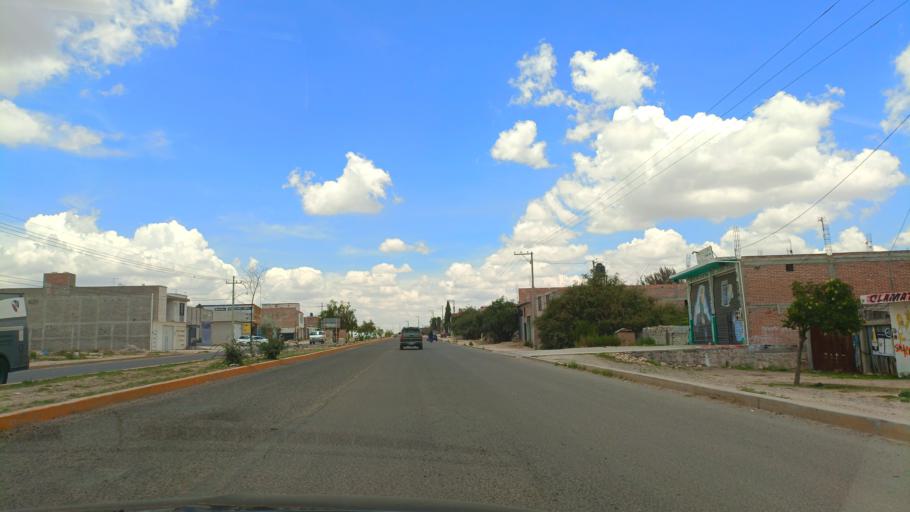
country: MX
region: Guanajuato
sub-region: San Luis de la Paz
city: San Luis de la Paz
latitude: 21.2899
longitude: -100.4940
